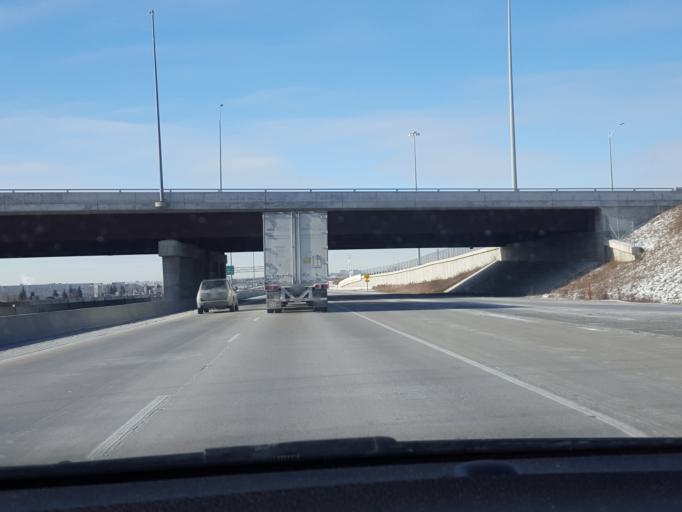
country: CA
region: Ontario
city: Mississauga
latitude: 43.6305
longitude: -79.6837
